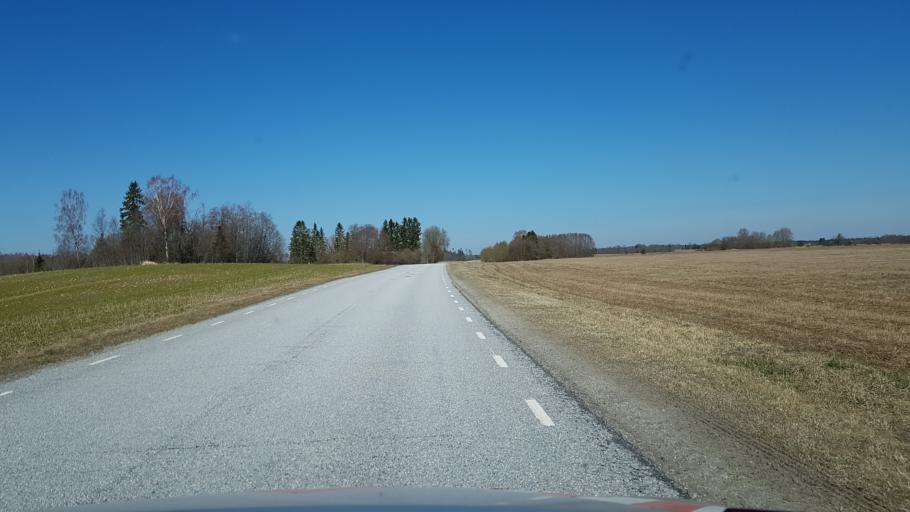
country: EE
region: Jaervamaa
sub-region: Koeru vald
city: Koeru
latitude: 59.0128
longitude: 26.0886
